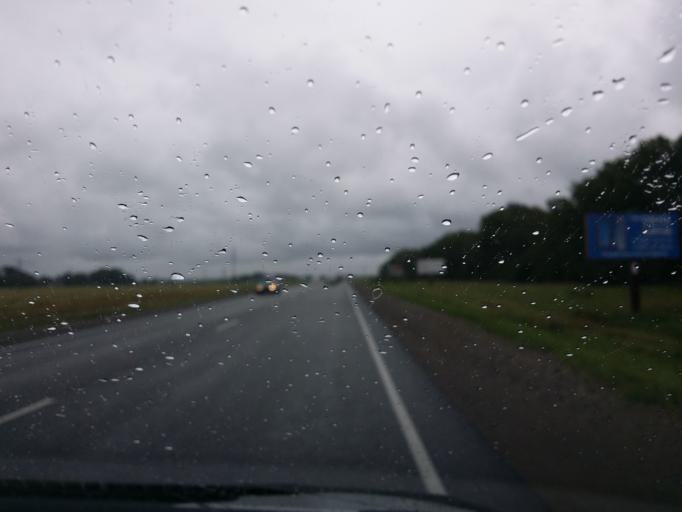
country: RU
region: Altai Krai
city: Zarya
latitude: 52.5952
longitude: 85.1503
